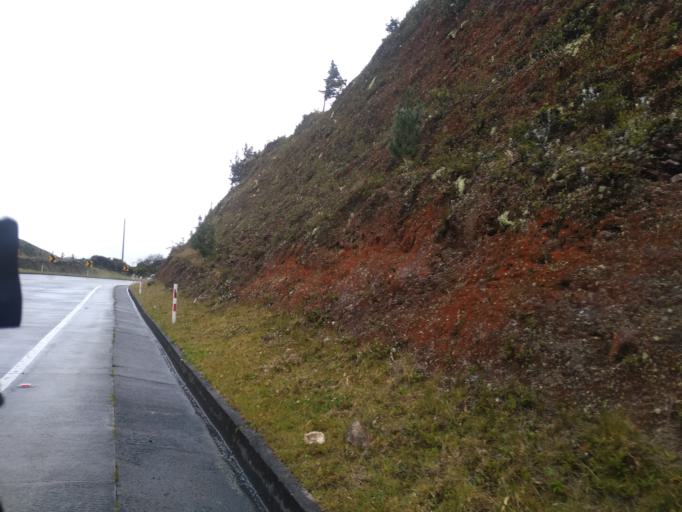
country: EC
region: Loja
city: Loja
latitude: -3.8932
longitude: -79.2618
